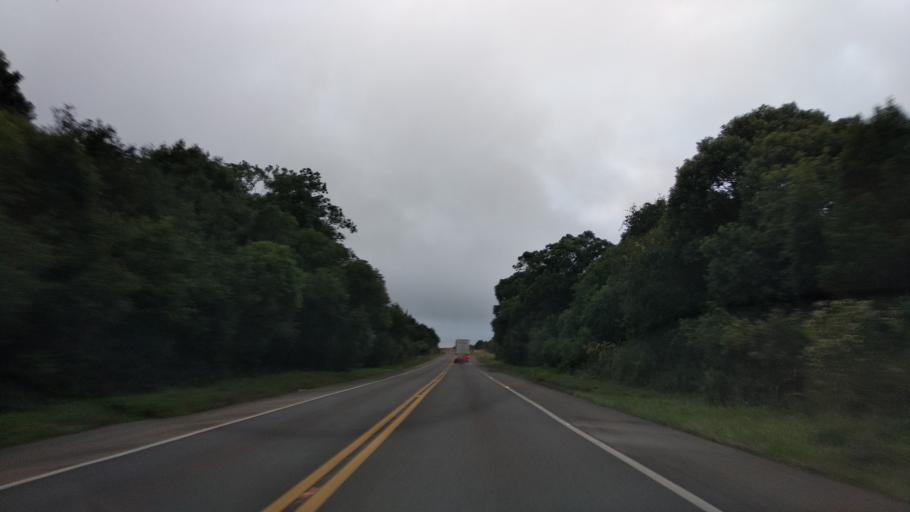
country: BR
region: Santa Catarina
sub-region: Campos Novos
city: Campos Novos
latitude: -27.3855
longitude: -51.1090
